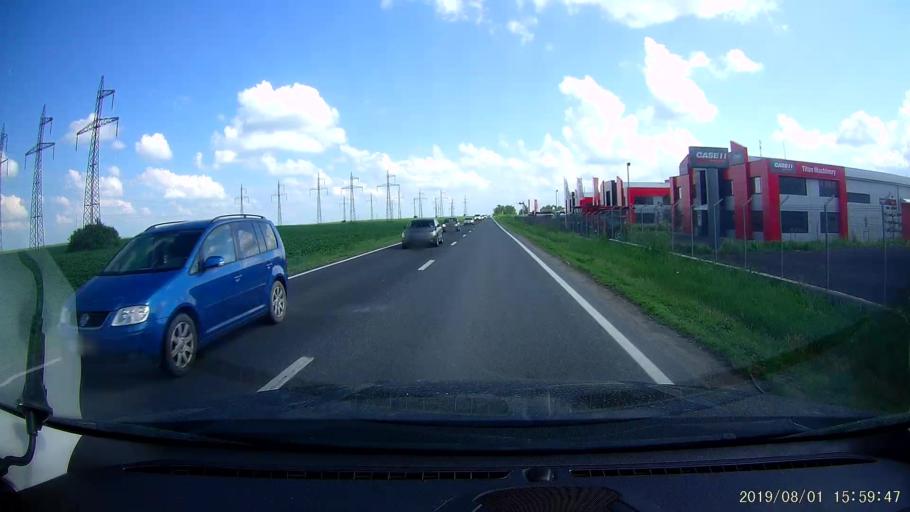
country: RO
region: Ialomita
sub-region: Comuna Slobozia
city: Slobozia
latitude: 44.5405
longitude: 27.3860
